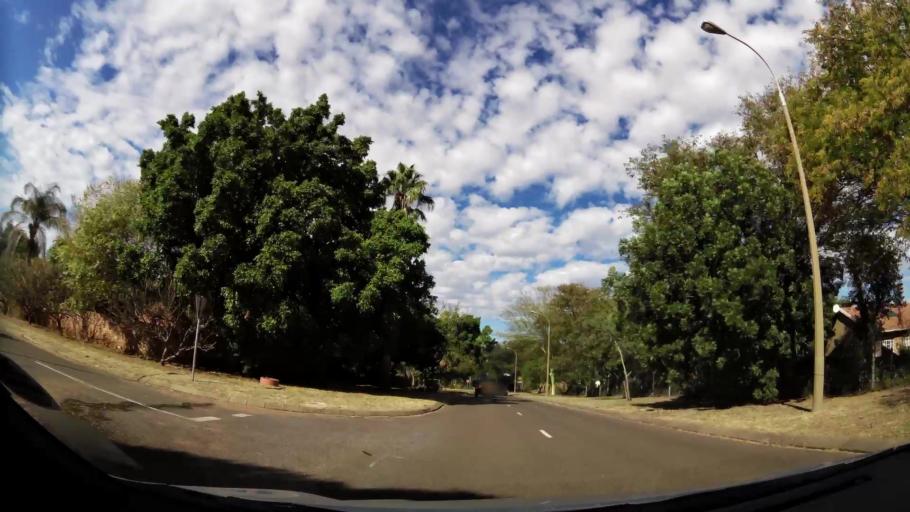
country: ZA
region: Limpopo
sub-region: Waterberg District Municipality
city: Warmbaths
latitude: -24.8726
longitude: 28.2865
